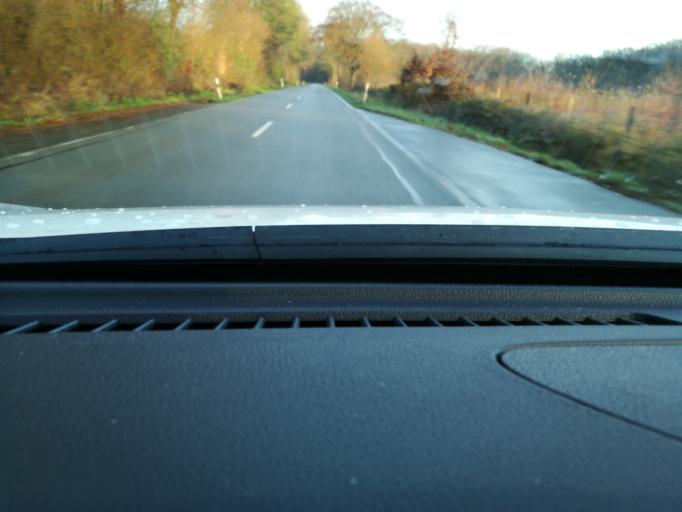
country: DE
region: Schleswig-Holstein
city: Ascheffel
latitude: 54.4169
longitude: 9.7033
